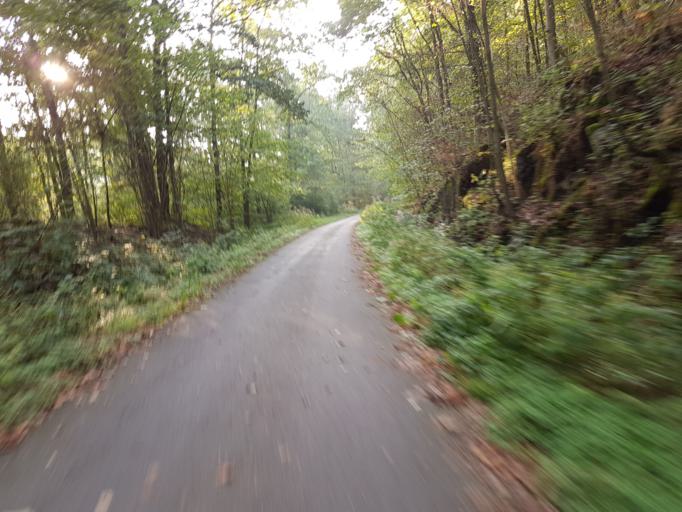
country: DE
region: Saxony
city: Taura
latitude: 50.9158
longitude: 12.8644
